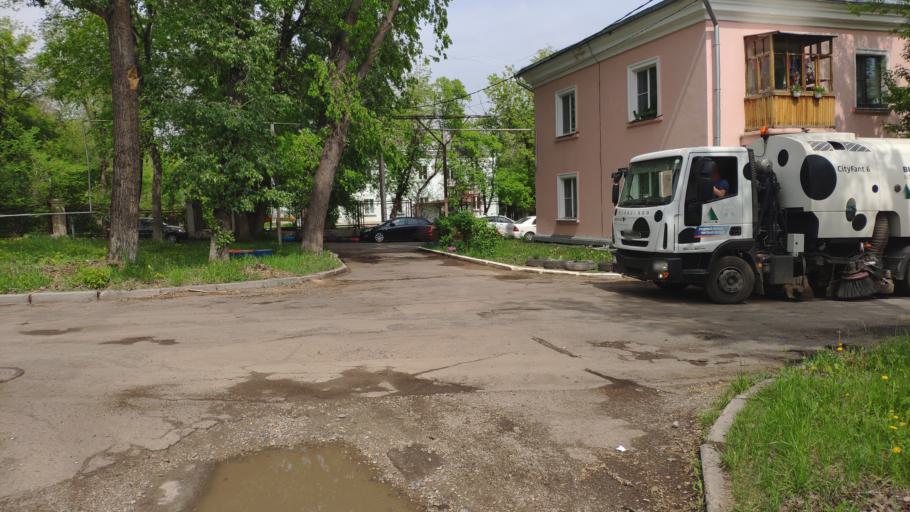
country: RU
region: Chelyabinsk
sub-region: Gorod Magnitogorsk
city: Magnitogorsk
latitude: 53.4212
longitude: 58.9560
